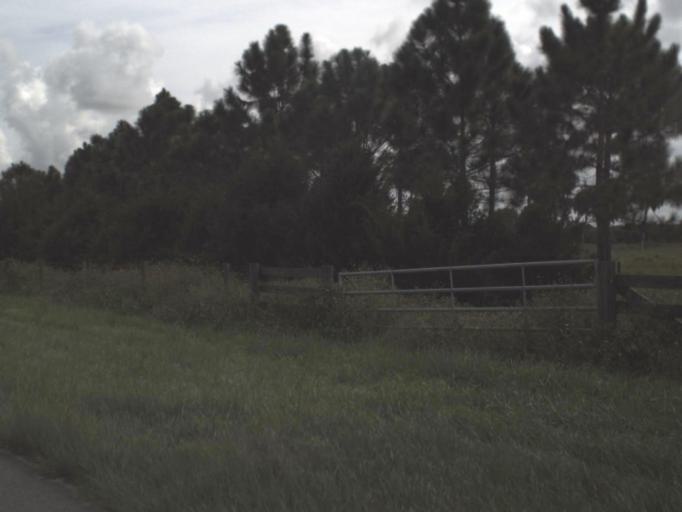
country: US
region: Florida
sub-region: Glades County
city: Buckhead Ridge
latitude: 27.2258
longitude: -81.0943
